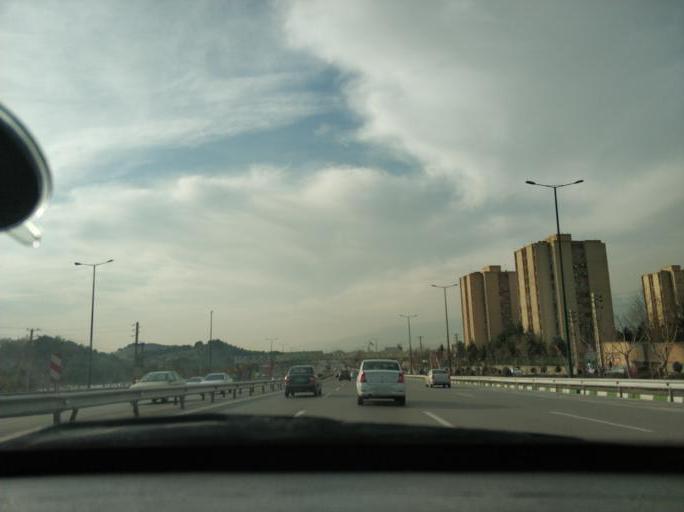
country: IR
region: Tehran
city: Tajrish
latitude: 35.7769
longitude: 51.5345
